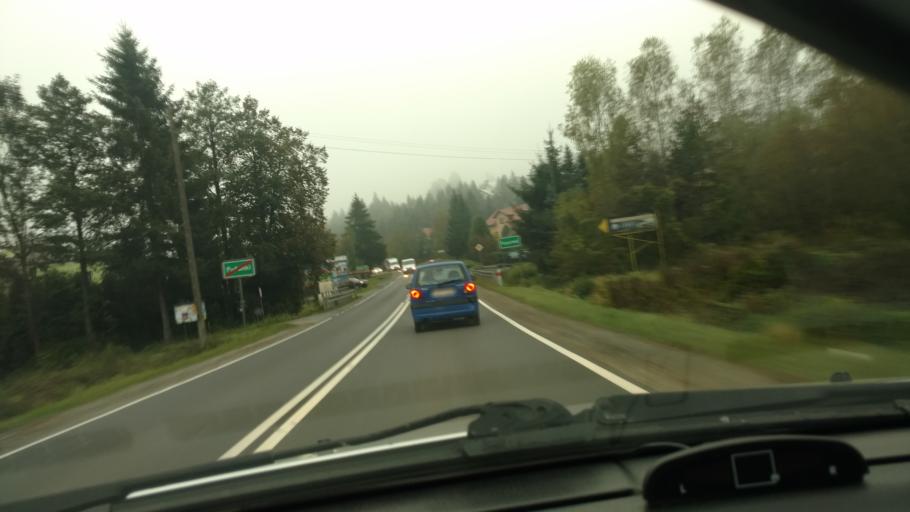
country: PL
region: Subcarpathian Voivodeship
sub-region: Powiat strzyzowski
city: Frysztak
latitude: 49.8409
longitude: 21.6096
